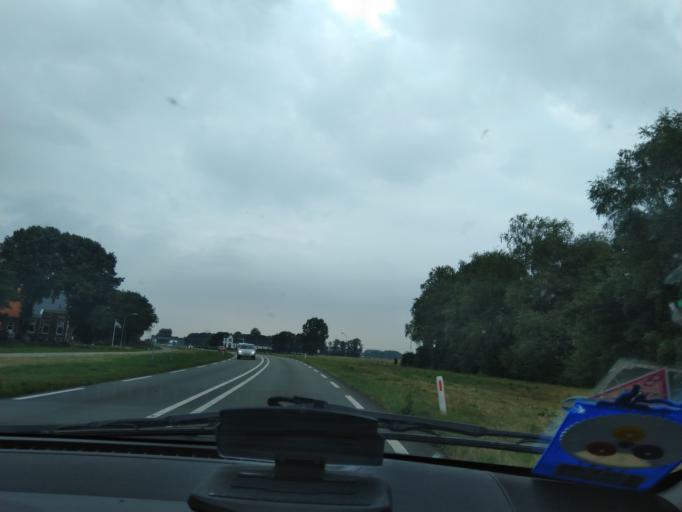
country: NL
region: Groningen
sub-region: Gemeente  Oldambt
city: Winschoten
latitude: 53.1125
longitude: 7.0644
